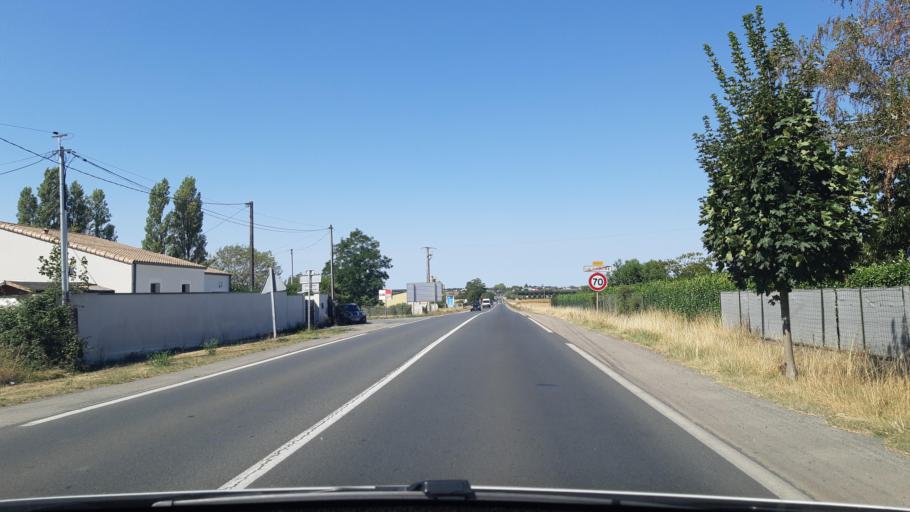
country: FR
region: Poitou-Charentes
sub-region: Departement des Deux-Sevres
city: La Creche
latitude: 46.3555
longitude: -0.3136
